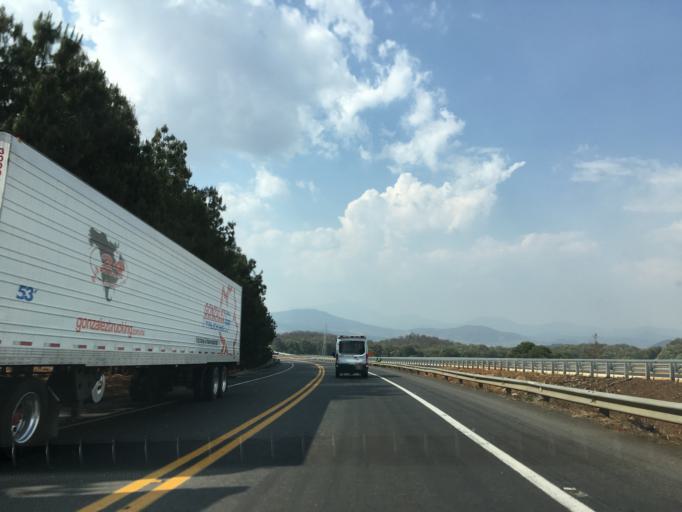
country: MX
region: Michoacan
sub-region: Patzcuaro
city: Colonia Vista Bella (Lomas del Peaje)
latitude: 19.5093
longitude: -101.5741
